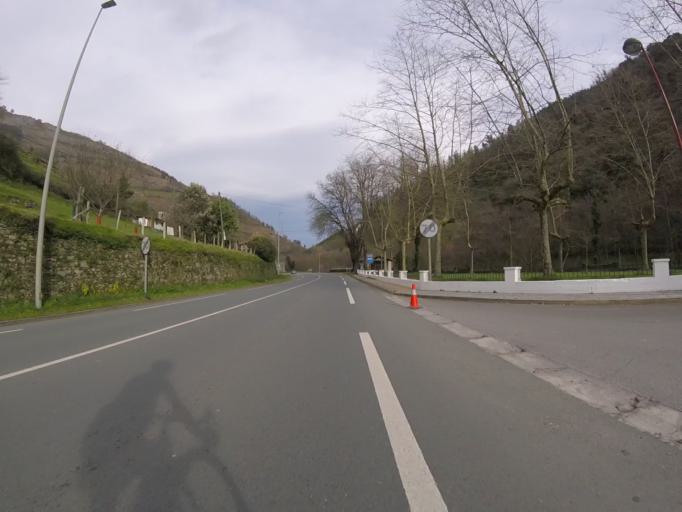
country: ES
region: Basque Country
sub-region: Provincia de Guipuzcoa
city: Azpeitia
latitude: 43.1900
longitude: -2.2590
